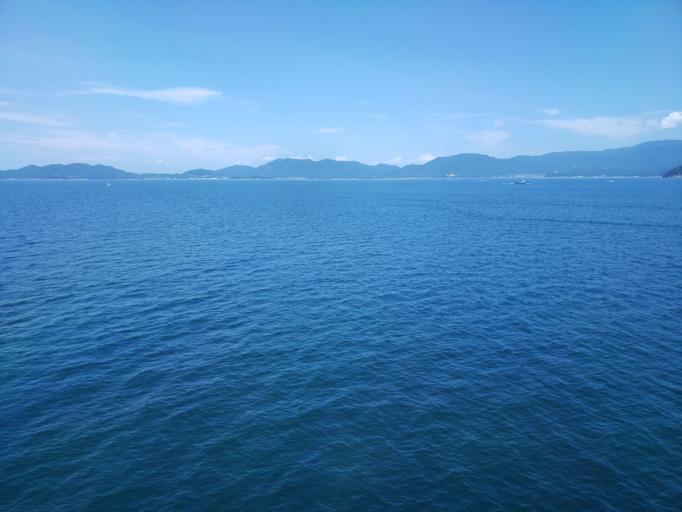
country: JP
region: Kagawa
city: Tonosho
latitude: 34.4076
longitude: 134.2023
